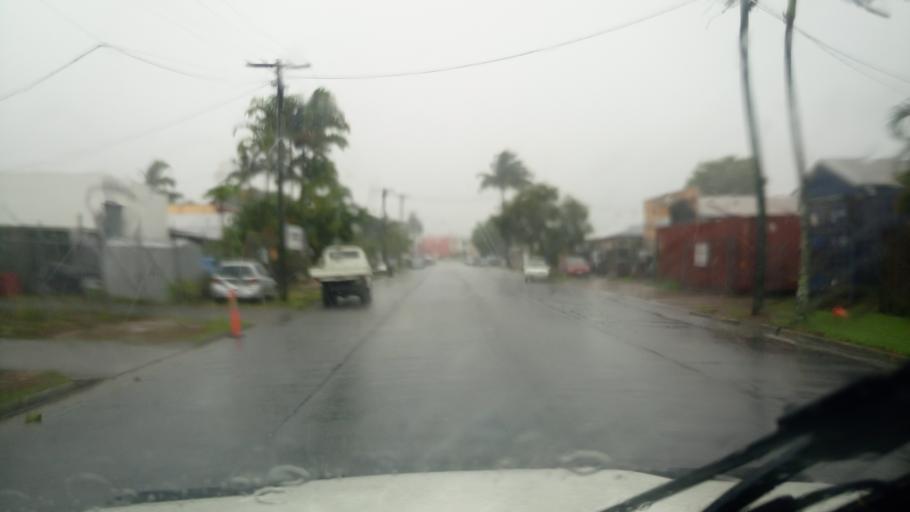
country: AU
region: Queensland
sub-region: Cairns
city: Cairns
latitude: -16.9380
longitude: 145.7607
